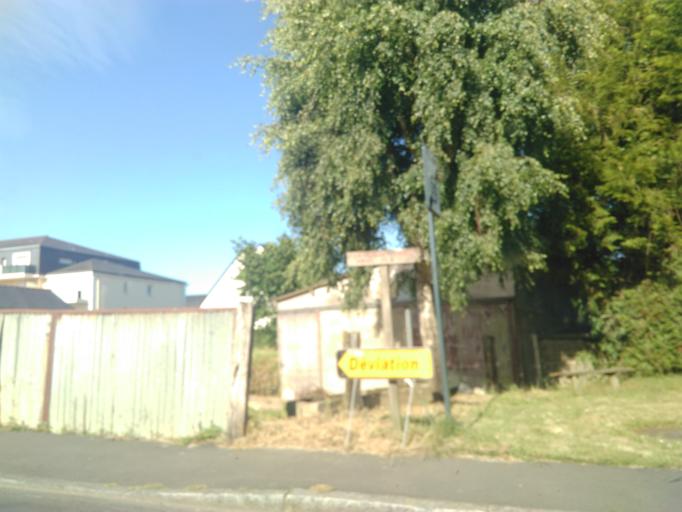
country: FR
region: Brittany
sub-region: Departement d'Ille-et-Vilaine
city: Pleumeleuc
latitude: 48.1856
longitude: -1.9194
